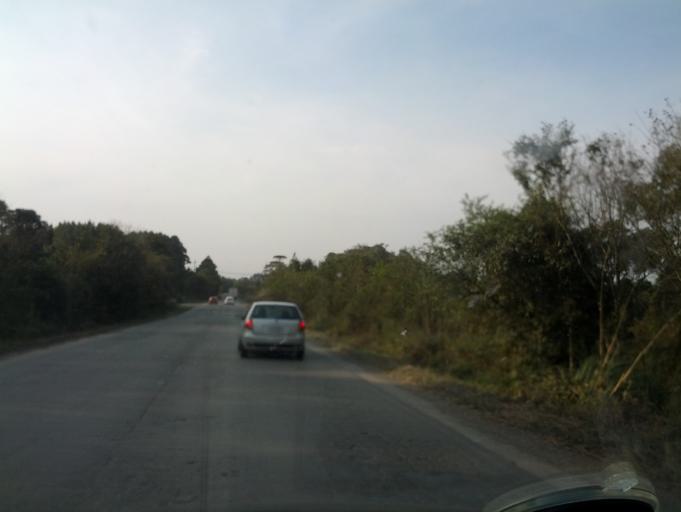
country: BR
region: Santa Catarina
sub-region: Otacilio Costa
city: Otacilio Costa
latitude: -27.5629
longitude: -50.1500
